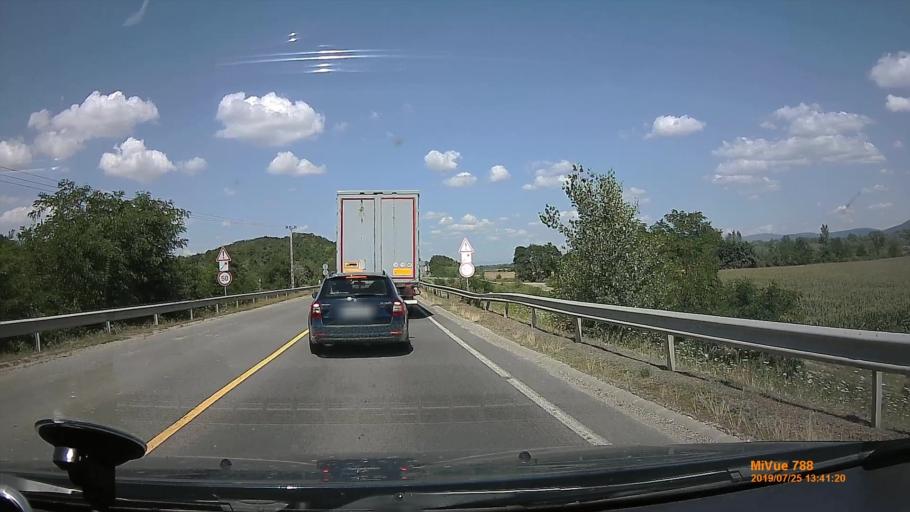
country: HU
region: Borsod-Abauj-Zemplen
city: Gonc
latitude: 48.4458
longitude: 21.1867
